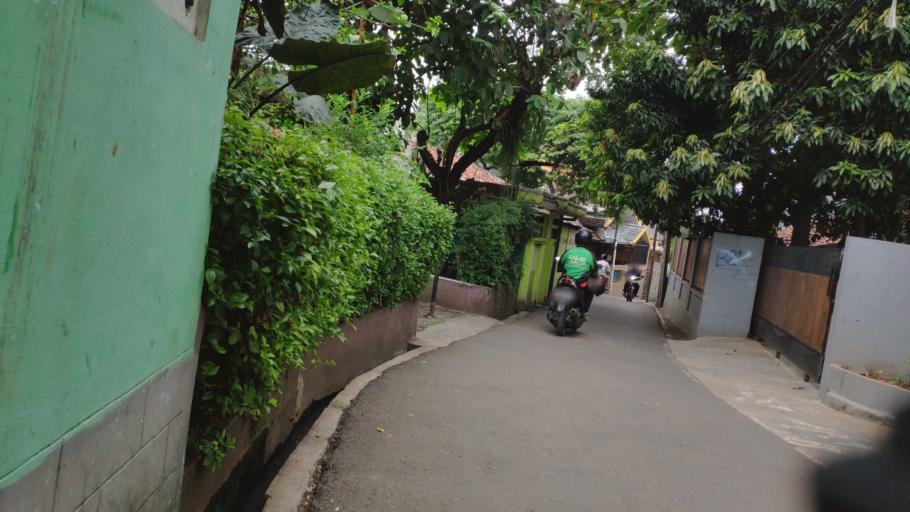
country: ID
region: West Java
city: Depok
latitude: -6.3152
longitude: 106.8339
